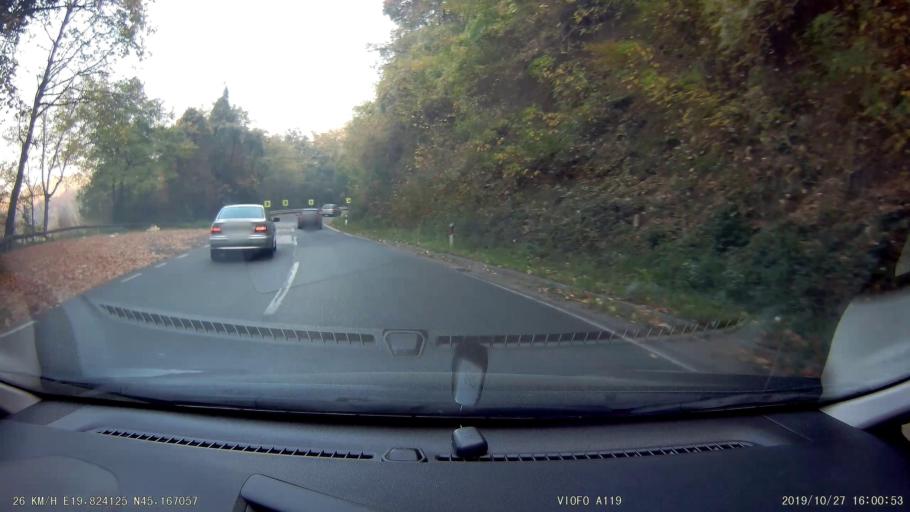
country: RS
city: Vrdnik
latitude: 45.1670
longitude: 19.8243
